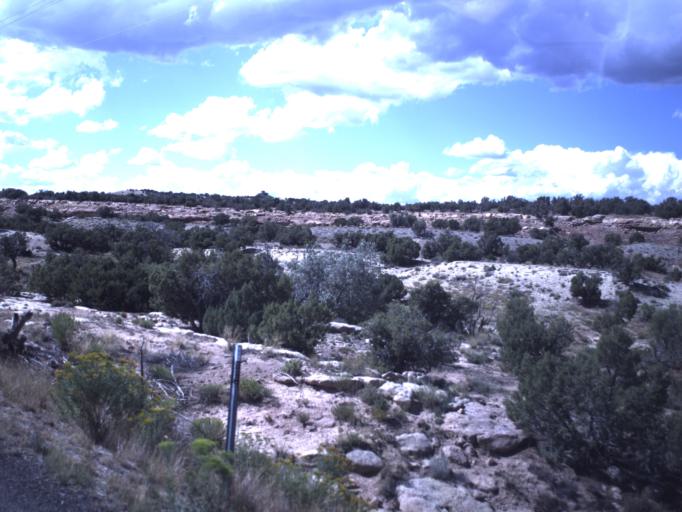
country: US
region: Utah
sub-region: Duchesne County
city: Duchesne
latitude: 40.1769
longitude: -110.4458
